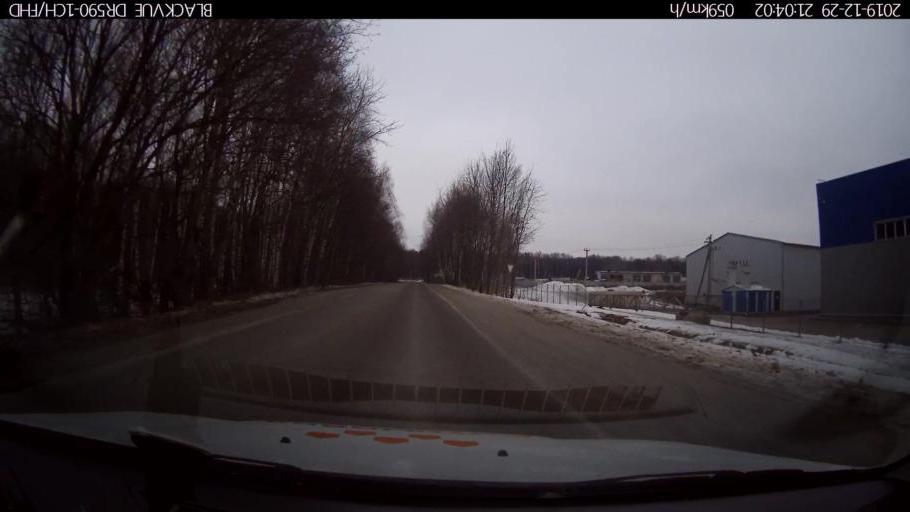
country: RU
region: Nizjnij Novgorod
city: Afonino
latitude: 56.2001
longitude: 44.0041
